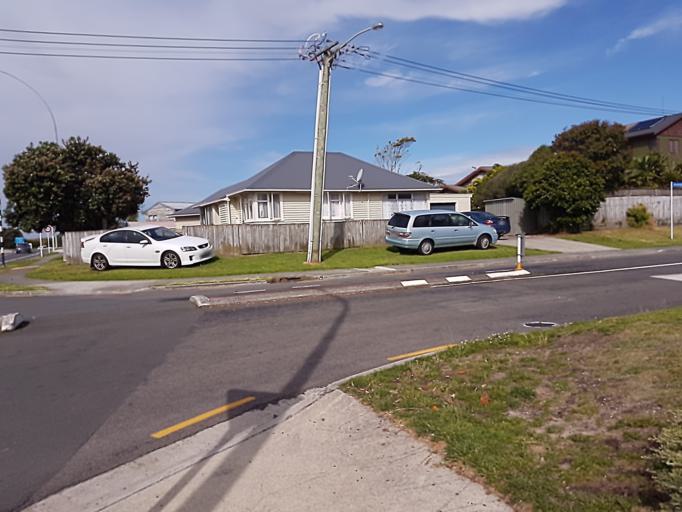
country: NZ
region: Bay of Plenty
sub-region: Western Bay of Plenty District
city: Maketu
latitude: -37.7095
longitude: 176.3165
